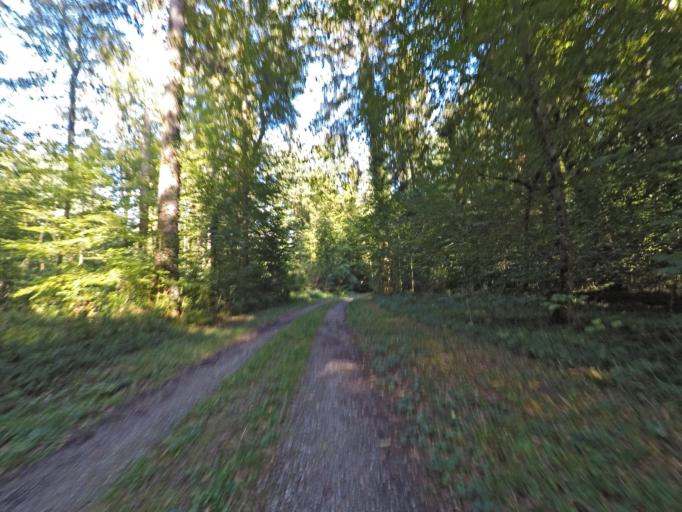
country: CH
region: Thurgau
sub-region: Frauenfeld District
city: Diessenhofen
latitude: 47.6549
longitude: 8.7436
